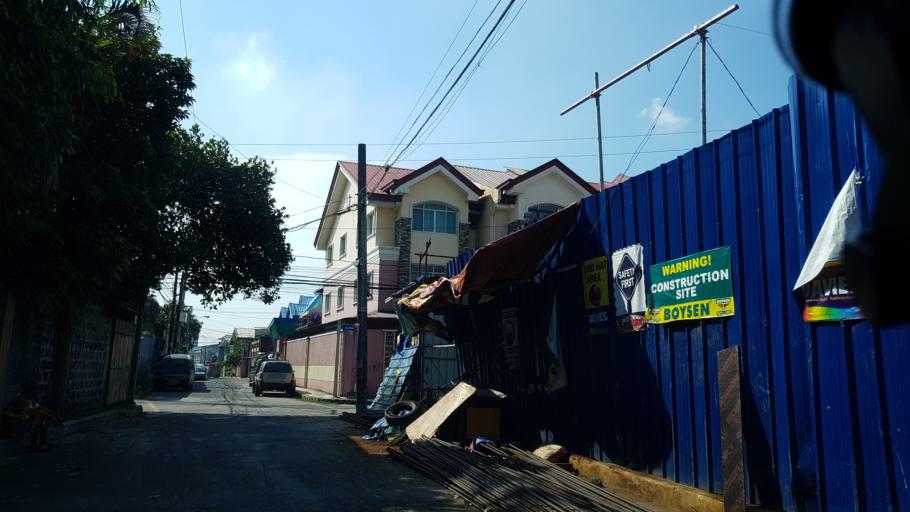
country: PH
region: Metro Manila
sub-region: Quezon City
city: Quezon City
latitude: 14.6253
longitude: 121.0438
